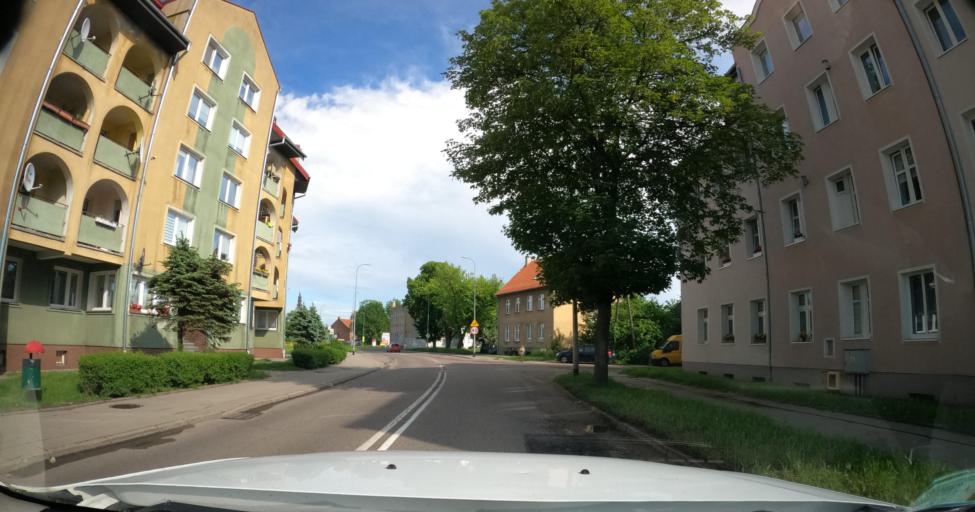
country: PL
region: Warmian-Masurian Voivodeship
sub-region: Powiat elblaski
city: Elblag
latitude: 54.1607
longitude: 19.3848
